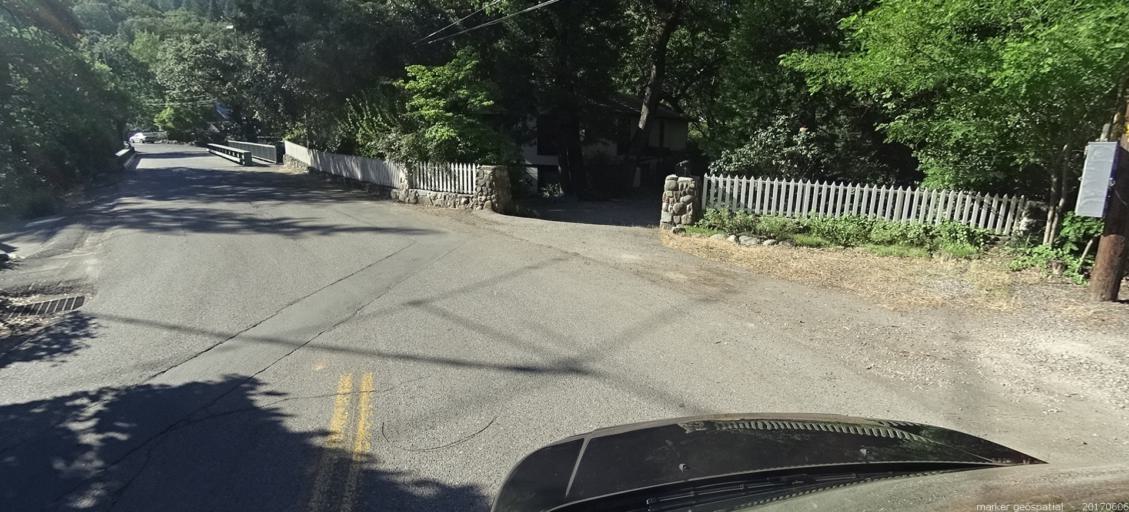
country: US
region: California
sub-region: Siskiyou County
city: Dunsmuir
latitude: 41.2025
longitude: -122.2732
